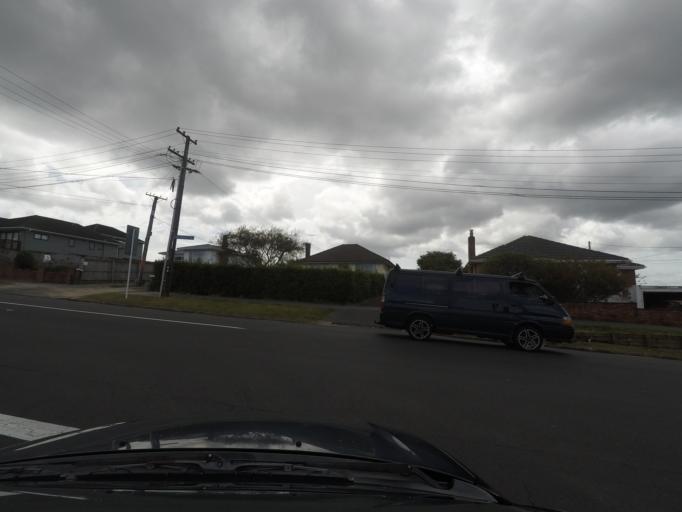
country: NZ
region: Auckland
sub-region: Auckland
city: Rosebank
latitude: -36.9083
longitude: 174.7146
